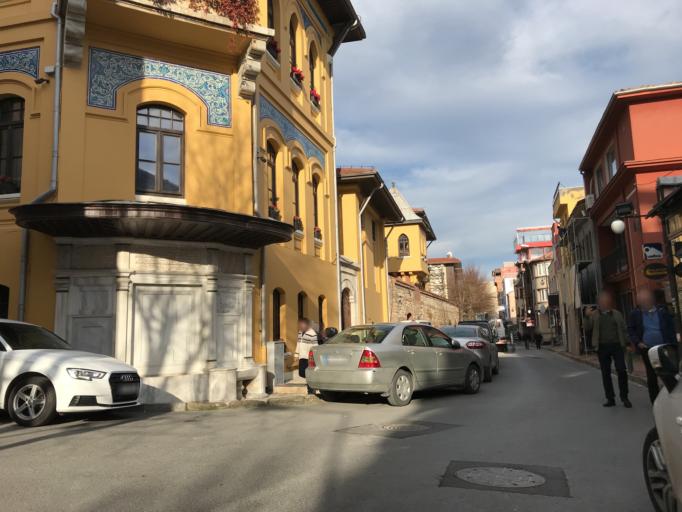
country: TR
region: Istanbul
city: Eminoenue
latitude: 41.0059
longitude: 28.9800
